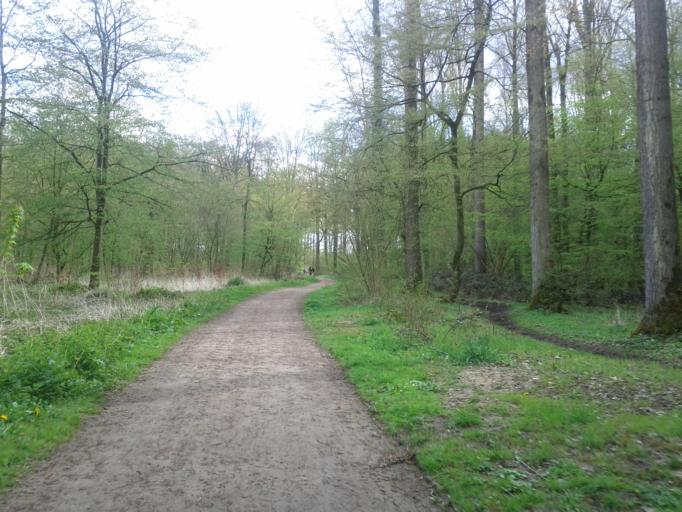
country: DE
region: North Rhine-Westphalia
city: Lanstrop
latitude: 51.5644
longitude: 7.5798
